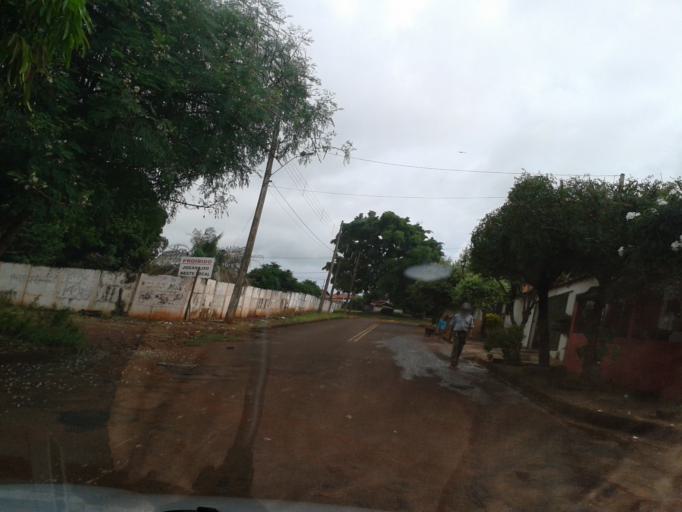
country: BR
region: Minas Gerais
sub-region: Ituiutaba
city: Ituiutaba
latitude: -18.9603
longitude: -49.4600
